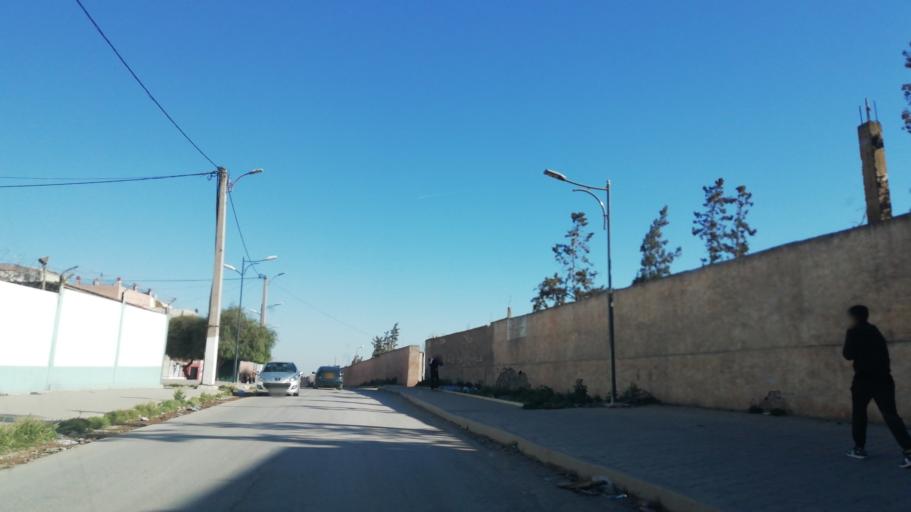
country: DZ
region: Oran
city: Bir el Djir
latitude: 35.7246
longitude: -0.5351
